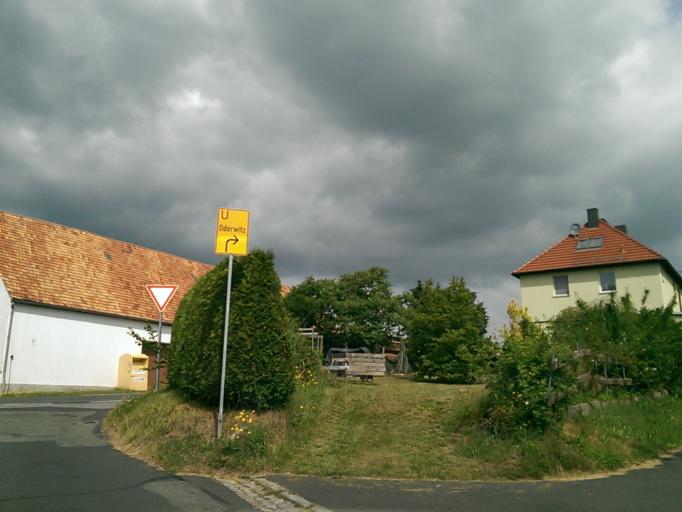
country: DE
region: Saxony
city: Mittelherwigsdorf
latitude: 50.9170
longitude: 14.7599
